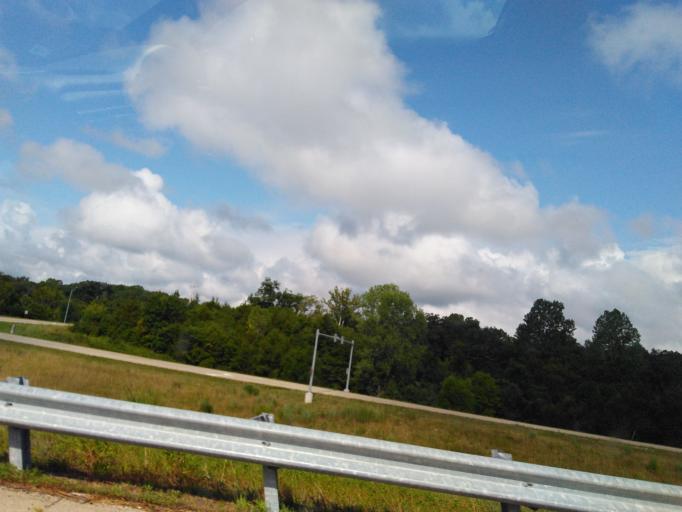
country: US
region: Missouri
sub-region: Jefferson County
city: Hillsboro
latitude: 38.2700
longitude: -90.5528
